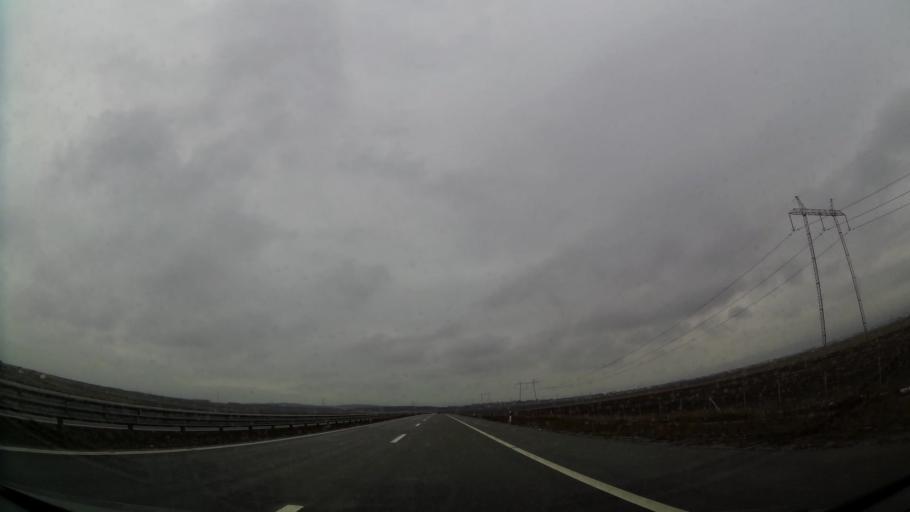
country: XK
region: Ferizaj
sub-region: Komuna e Ferizajt
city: Ferizaj
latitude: 42.3943
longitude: 21.1992
